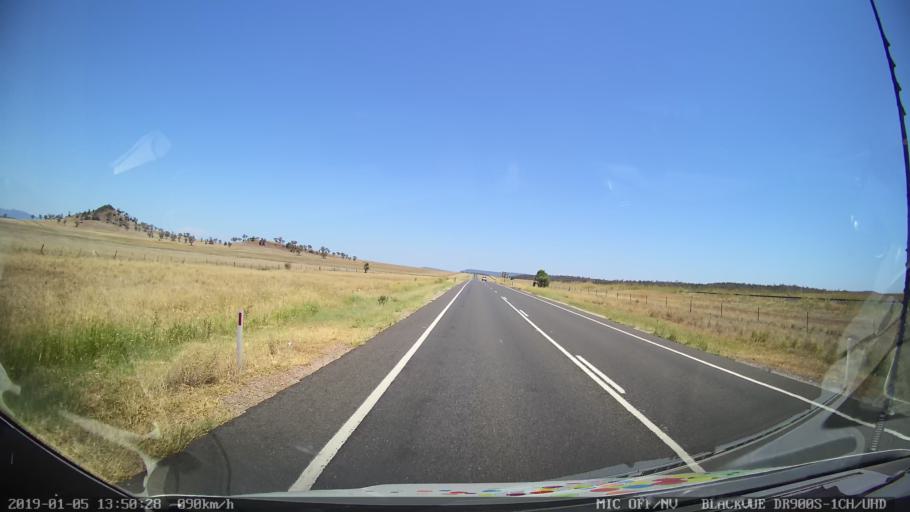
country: AU
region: New South Wales
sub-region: Gunnedah
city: Gunnedah
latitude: -31.0305
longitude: 150.2750
